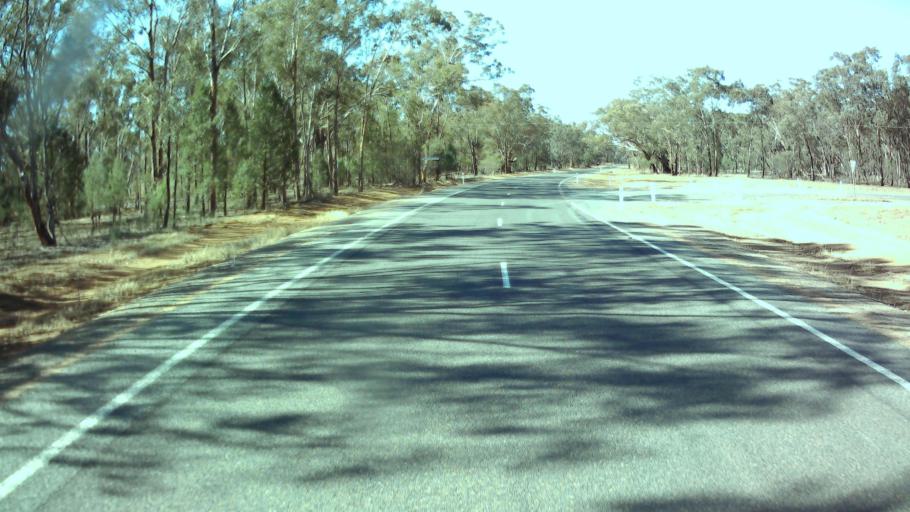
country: AU
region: New South Wales
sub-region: Weddin
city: Grenfell
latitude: -33.7549
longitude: 148.0828
